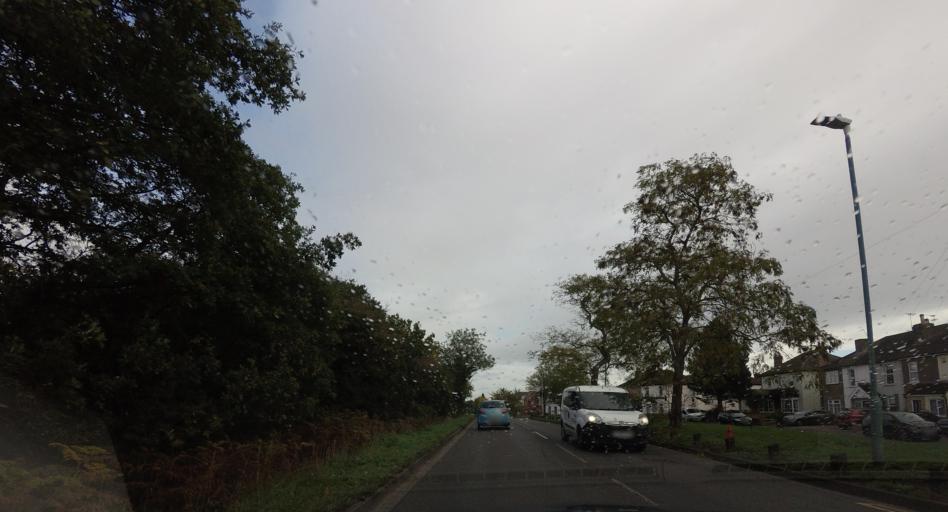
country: GB
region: England
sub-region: Kent
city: Swanley
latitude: 51.4315
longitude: 0.1847
